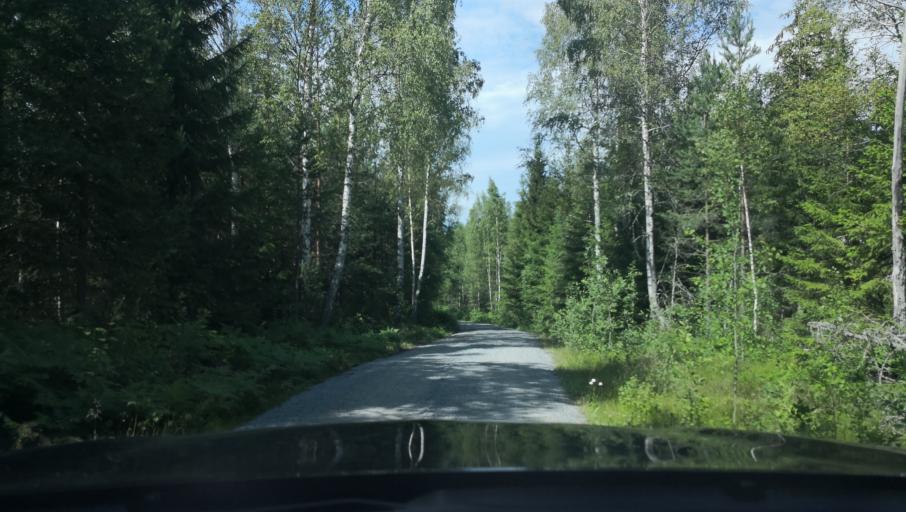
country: SE
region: Vaestmanland
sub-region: Surahammars Kommun
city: Ramnas
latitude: 59.9416
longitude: 16.1909
